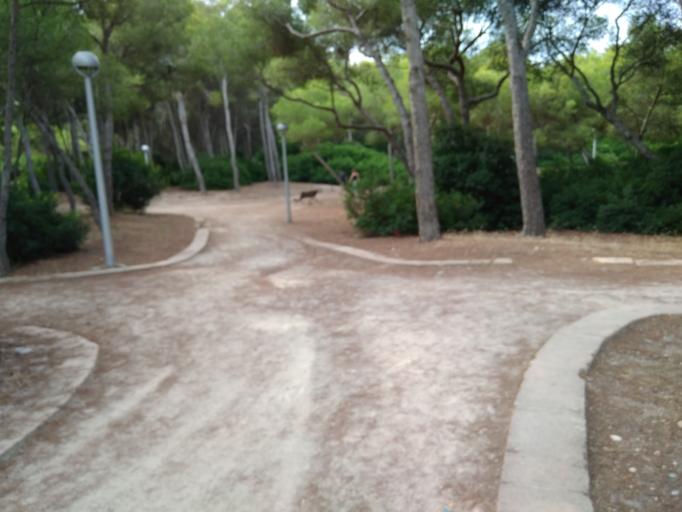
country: ES
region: Balearic Islands
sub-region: Illes Balears
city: s'Arenal
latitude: 39.5287
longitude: 2.7378
